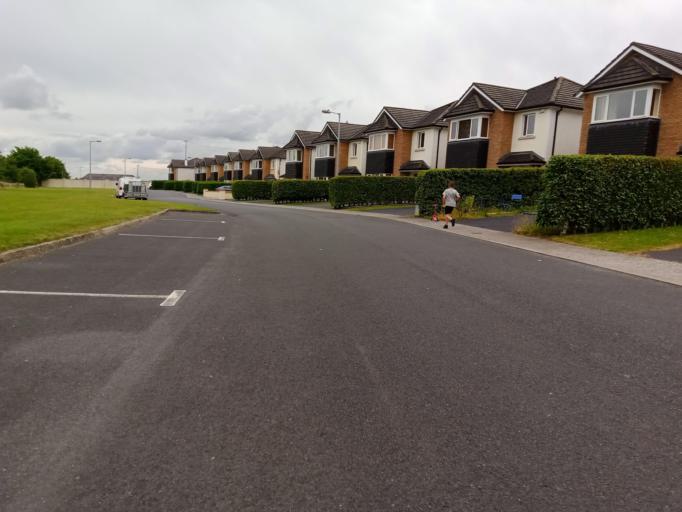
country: IE
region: Leinster
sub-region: Kilkenny
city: Callan
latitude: 52.5390
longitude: -7.3911
